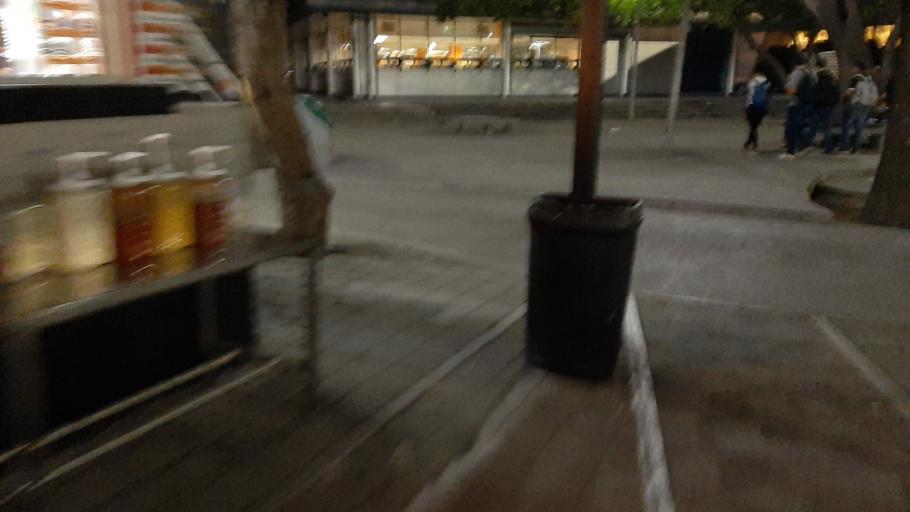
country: MX
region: Nuevo Leon
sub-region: San Nicolas de los Garza
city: San Nicolas de los Garza
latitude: 25.7254
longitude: -100.3113
